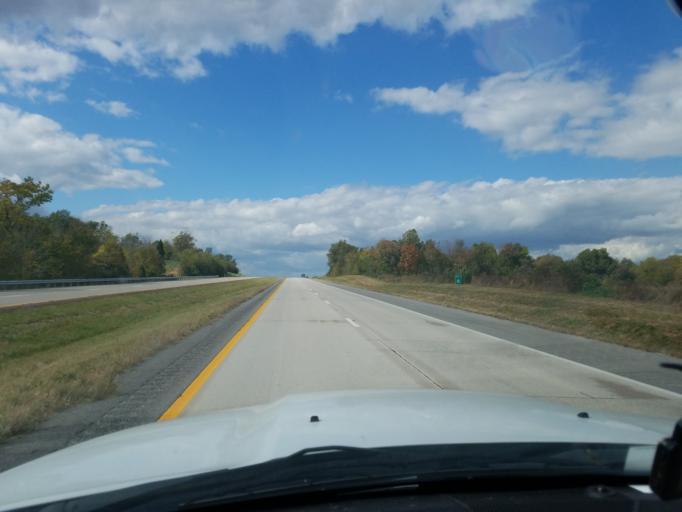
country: US
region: Kentucky
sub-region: Henderson County
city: Henderson
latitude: 37.7826
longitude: -87.4607
